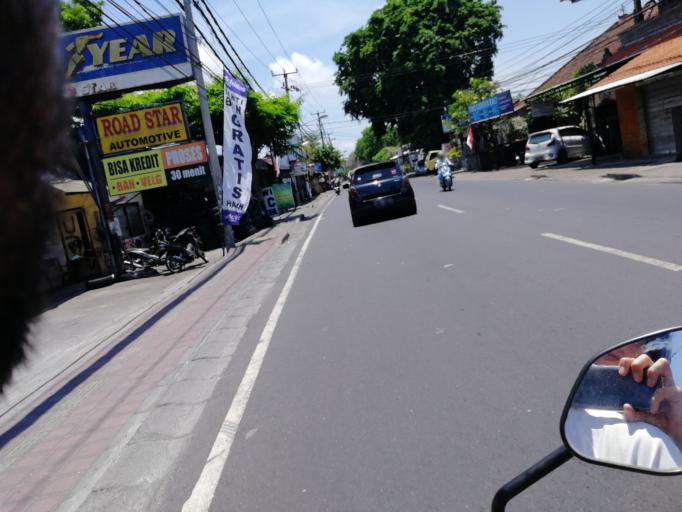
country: ID
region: Bali
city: Karyadharma
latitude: -8.6852
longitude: 115.1944
